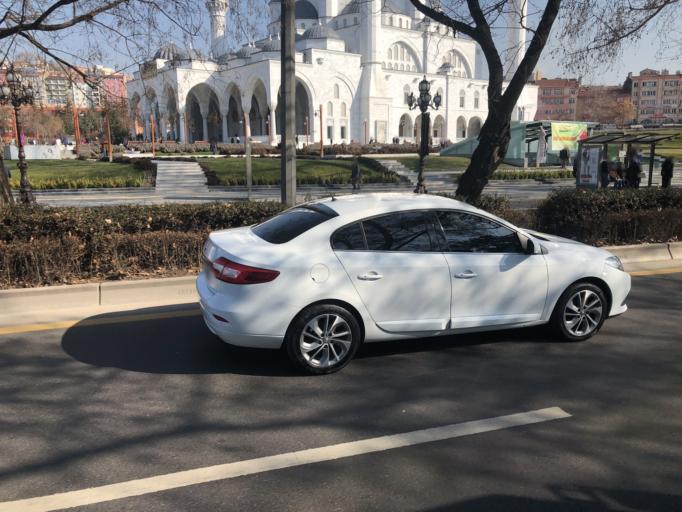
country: TR
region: Ankara
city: Ankara
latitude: 39.9368
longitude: 32.8543
